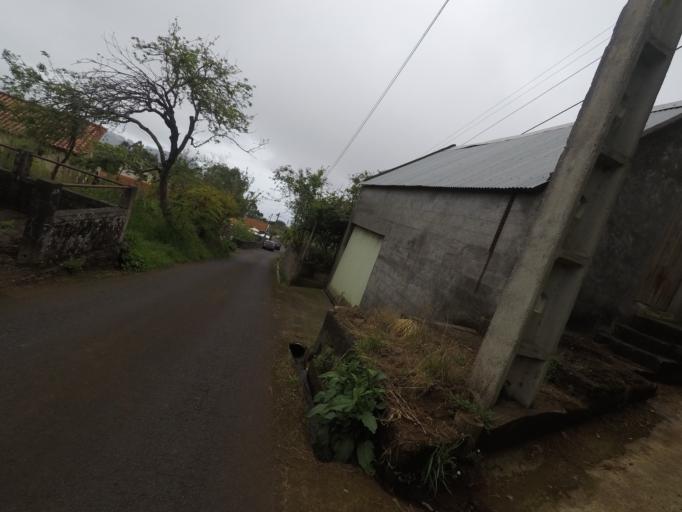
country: PT
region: Madeira
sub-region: Santana
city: Santana
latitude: 32.7526
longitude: -16.8728
